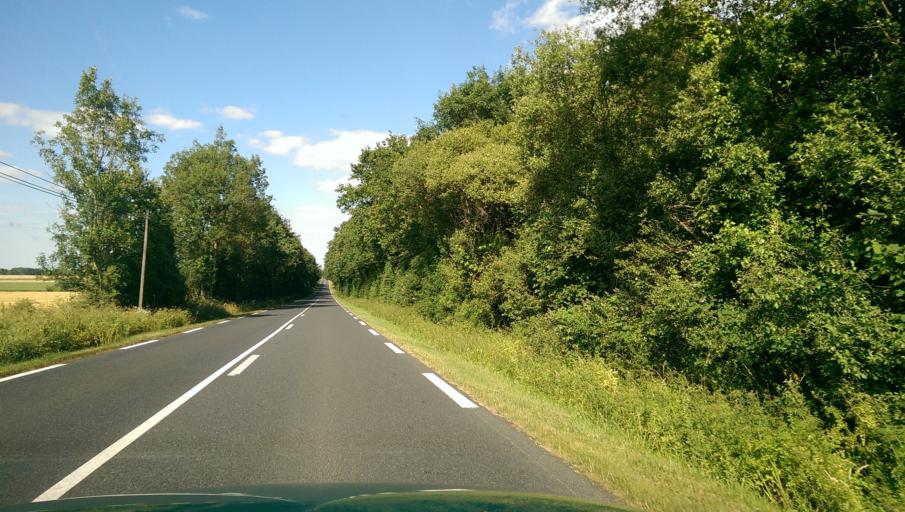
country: FR
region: Pays de la Loire
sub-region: Departement de la Vendee
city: Rocheserviere
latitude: 46.9476
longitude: -1.4877
